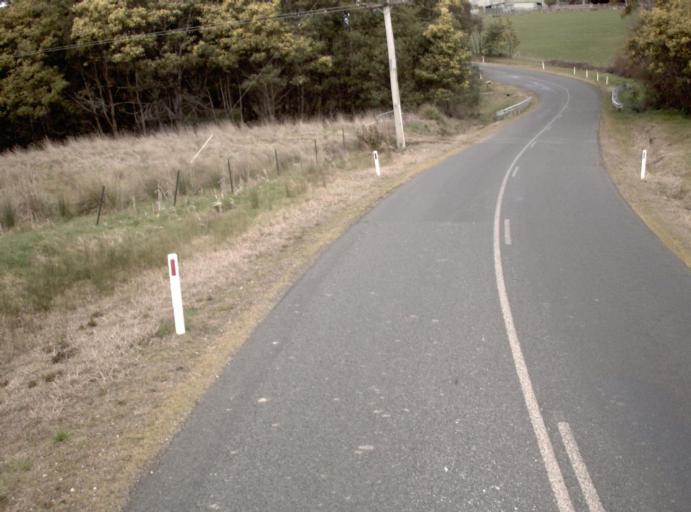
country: AU
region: Tasmania
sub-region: Launceston
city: Mayfield
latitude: -41.2059
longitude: 147.1178
